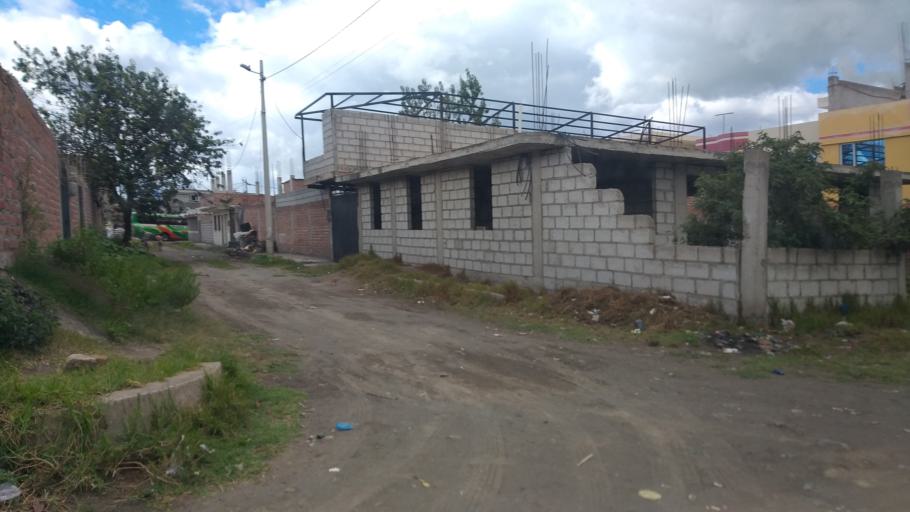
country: EC
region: Chimborazo
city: Riobamba
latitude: -1.6905
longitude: -78.6277
